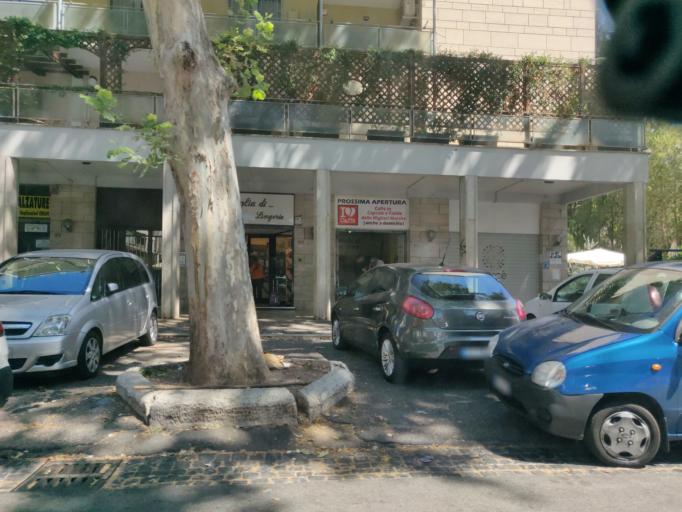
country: IT
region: Latium
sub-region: Citta metropolitana di Roma Capitale
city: Selcetta
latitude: 41.8263
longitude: 12.4773
